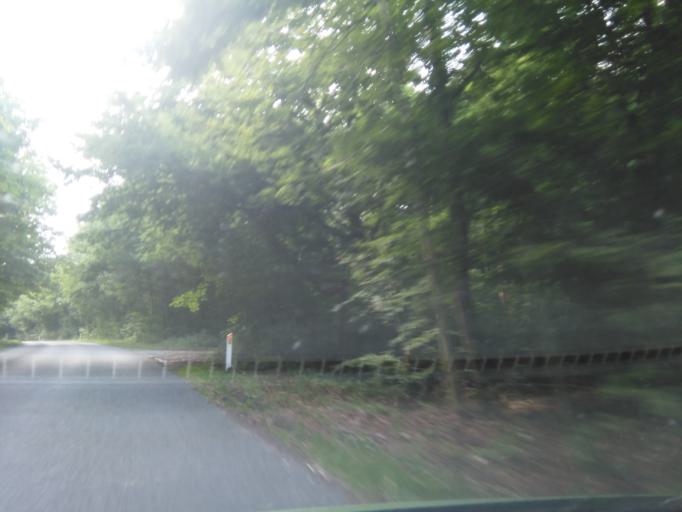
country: DK
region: Central Jutland
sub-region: Skanderborg Kommune
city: Horning
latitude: 56.1100
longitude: 10.0166
